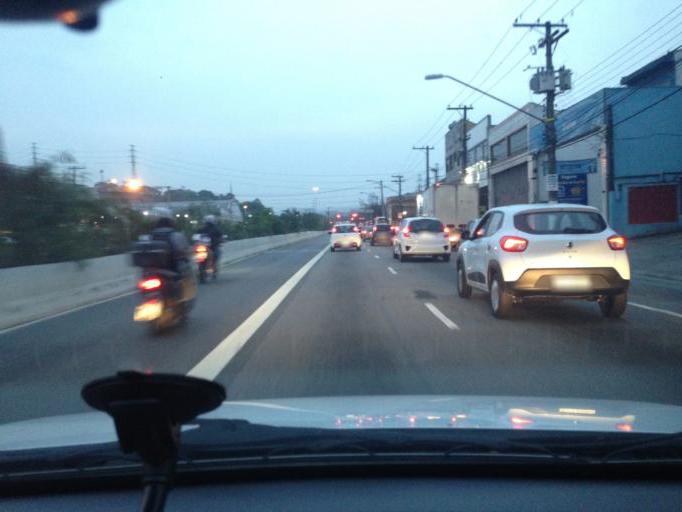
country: BR
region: Sao Paulo
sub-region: Sao Paulo
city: Sao Paulo
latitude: -23.5044
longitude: -46.7061
